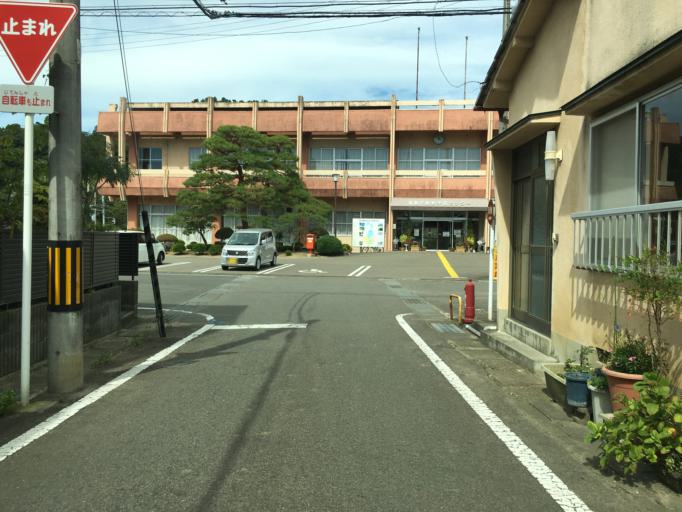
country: JP
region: Fukushima
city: Fukushima-shi
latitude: 37.6568
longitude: 140.5396
